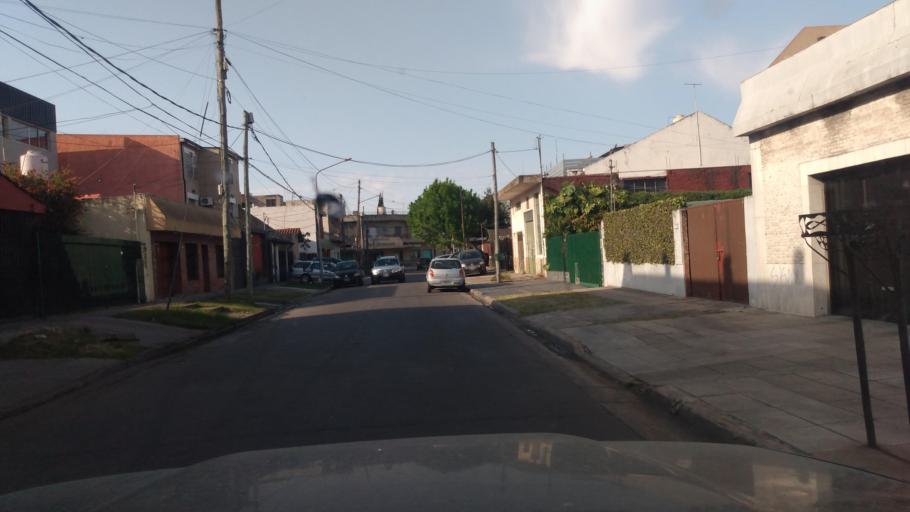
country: AR
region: Buenos Aires
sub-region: Partido de Moron
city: Moron
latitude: -34.6337
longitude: -58.6191
